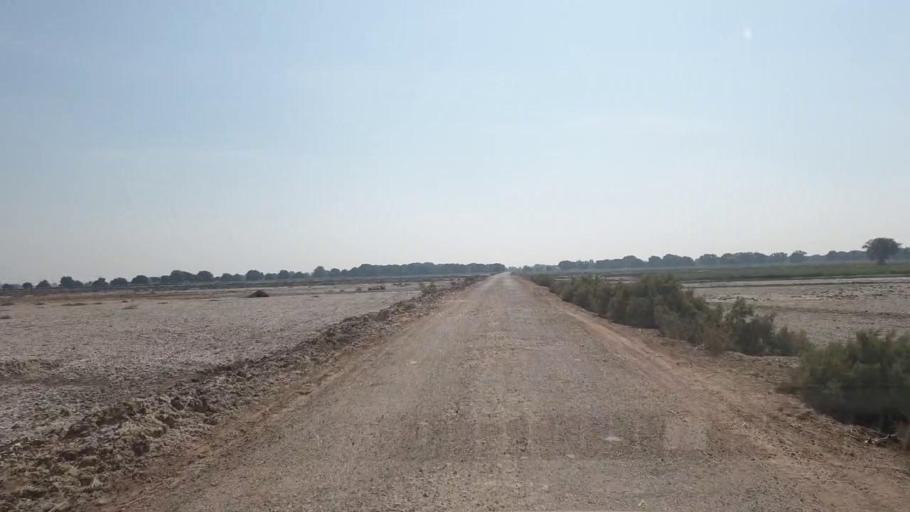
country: PK
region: Sindh
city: Chambar
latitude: 25.3835
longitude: 68.8033
